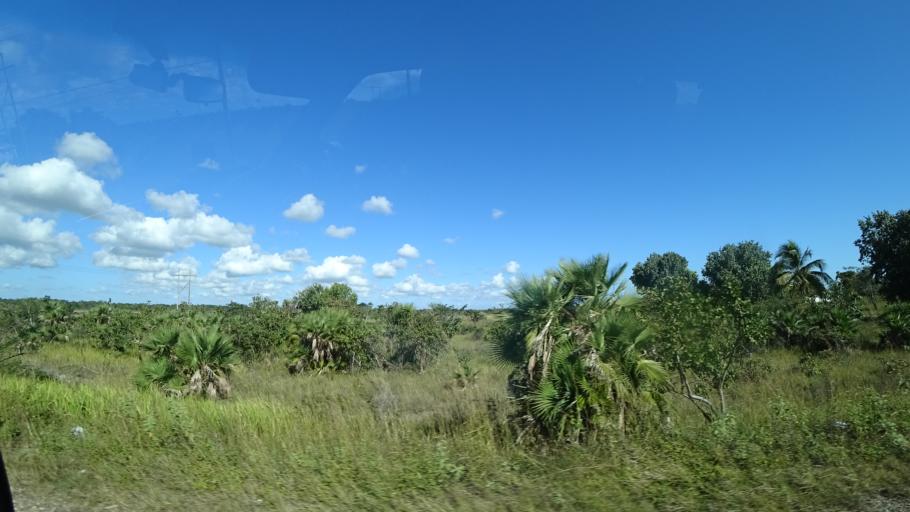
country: BZ
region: Belize
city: Belize City
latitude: 17.5821
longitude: -88.3614
